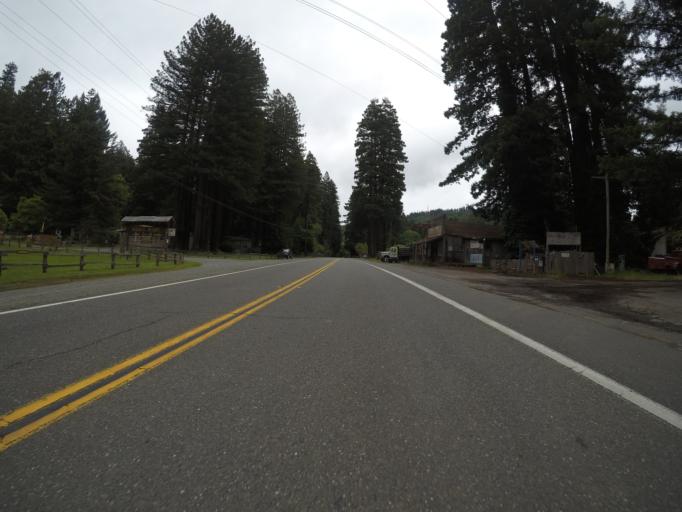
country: US
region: California
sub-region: Humboldt County
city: Rio Dell
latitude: 40.4009
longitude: -123.9499
